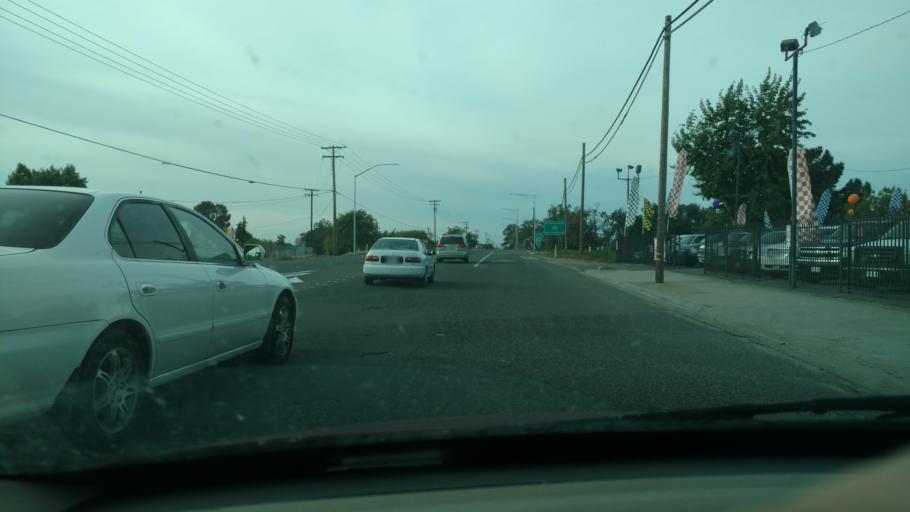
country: US
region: California
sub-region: Stanislaus County
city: Shackelford
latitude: 37.6167
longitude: -120.9936
